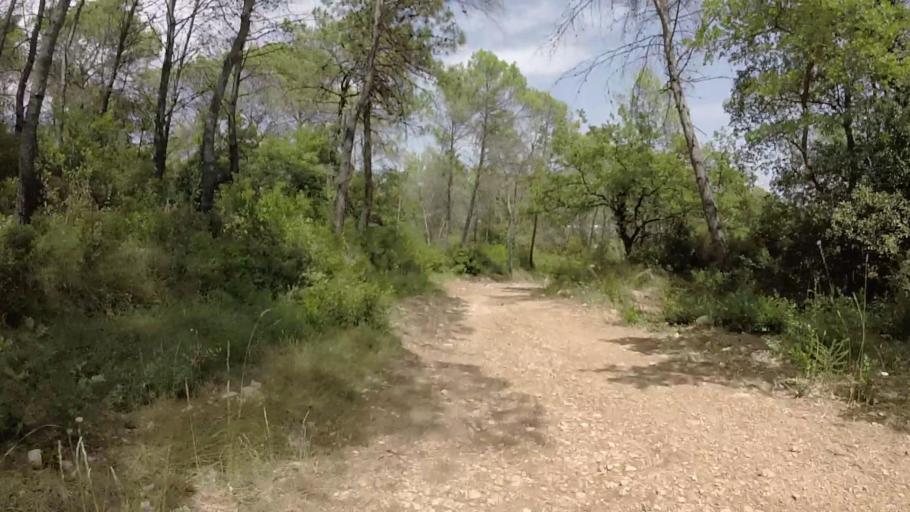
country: FR
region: Provence-Alpes-Cote d'Azur
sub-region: Departement des Alpes-Maritimes
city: Mougins
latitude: 43.6166
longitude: 7.0365
